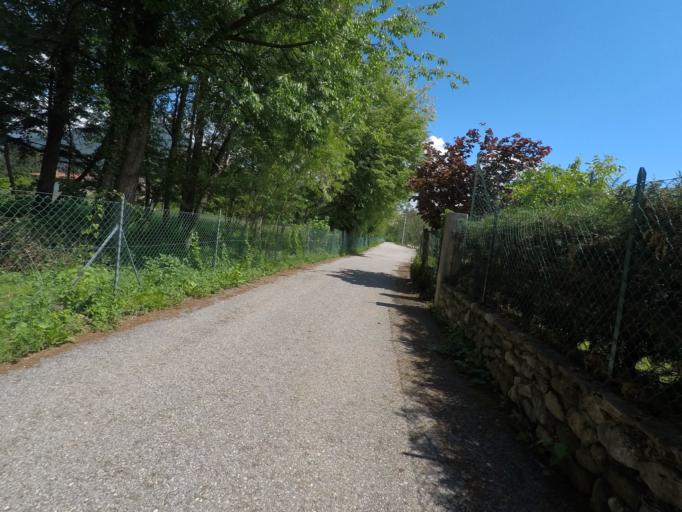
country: IT
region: Friuli Venezia Giulia
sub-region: Provincia di Udine
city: Chiaulis
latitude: 46.4049
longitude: 12.9854
